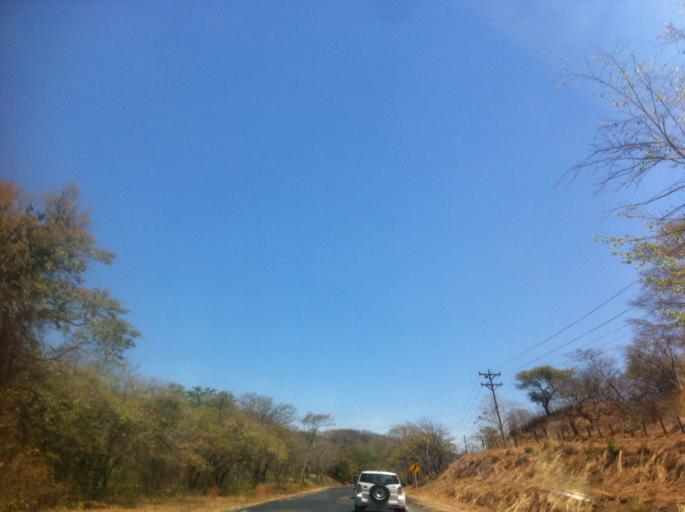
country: CR
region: Guanacaste
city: Belen
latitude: 10.3685
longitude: -85.5772
